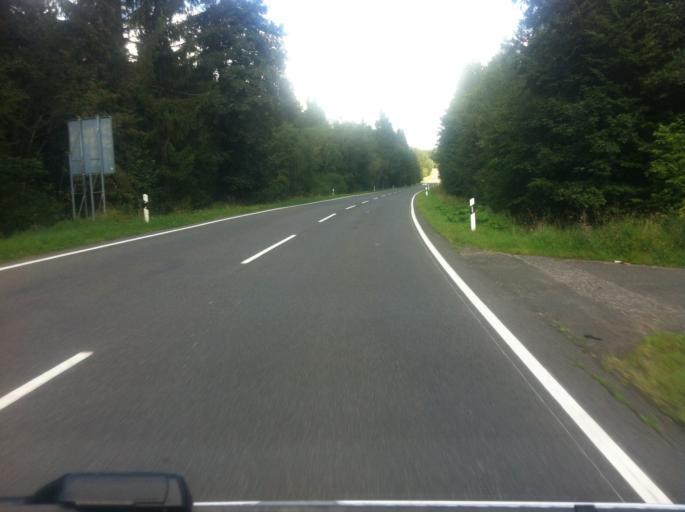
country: DE
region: Rheinland-Pfalz
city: Scheid
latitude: 50.3852
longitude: 6.3472
